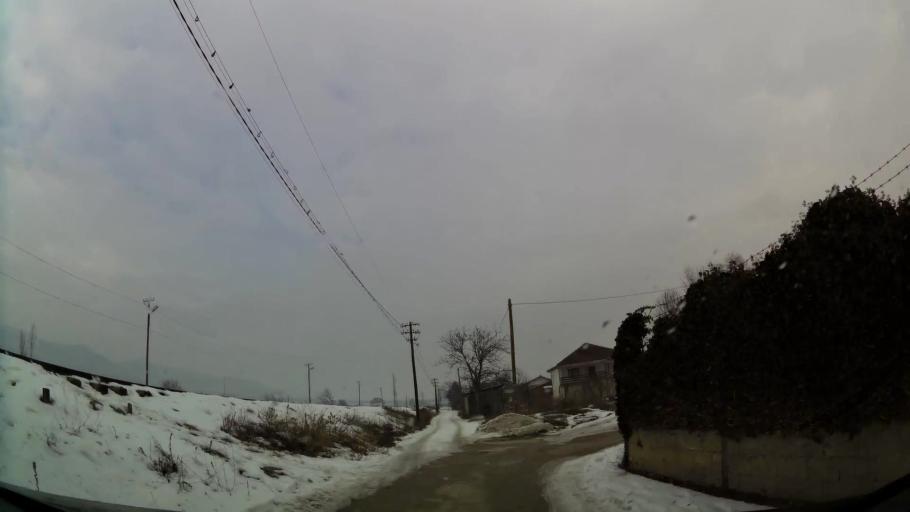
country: MK
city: Kondovo
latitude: 42.0490
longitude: 21.3547
